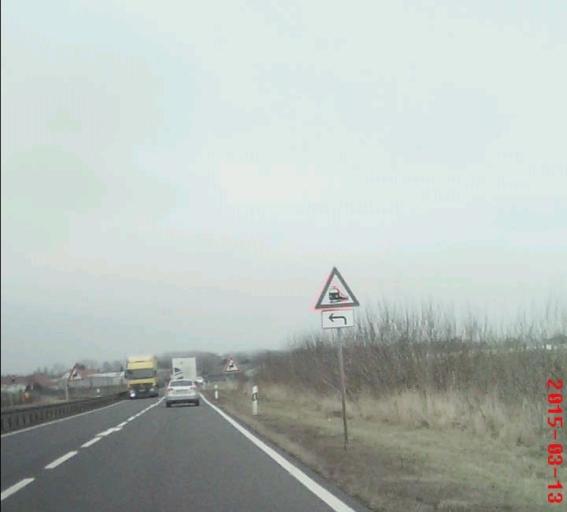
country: DE
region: Thuringia
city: Dollstadt
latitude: 51.0849
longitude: 10.8006
